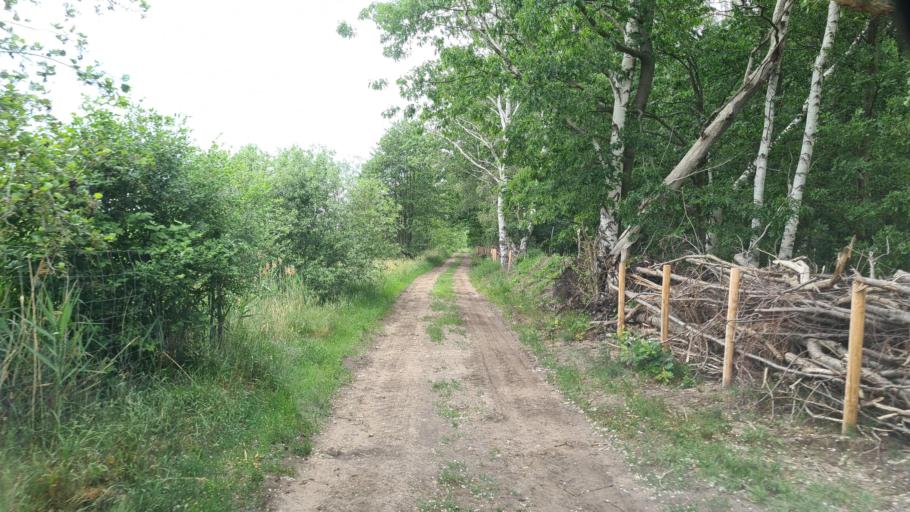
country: DE
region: Brandenburg
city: Bronkow
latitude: 51.6241
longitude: 13.9248
